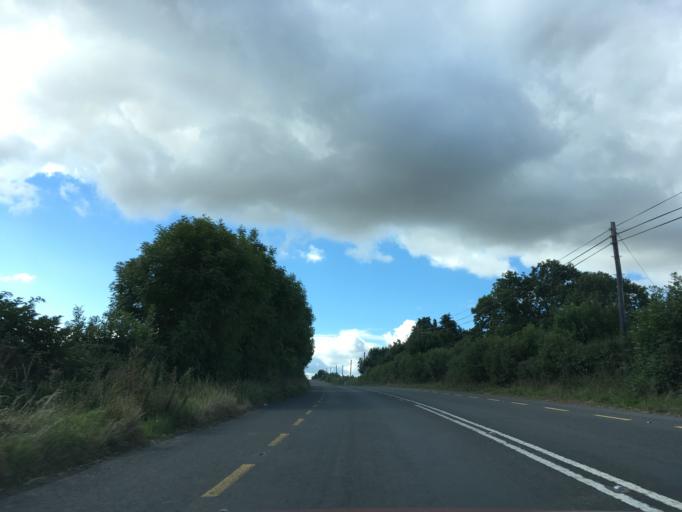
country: IE
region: Munster
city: Cahir
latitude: 52.4239
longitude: -7.8881
